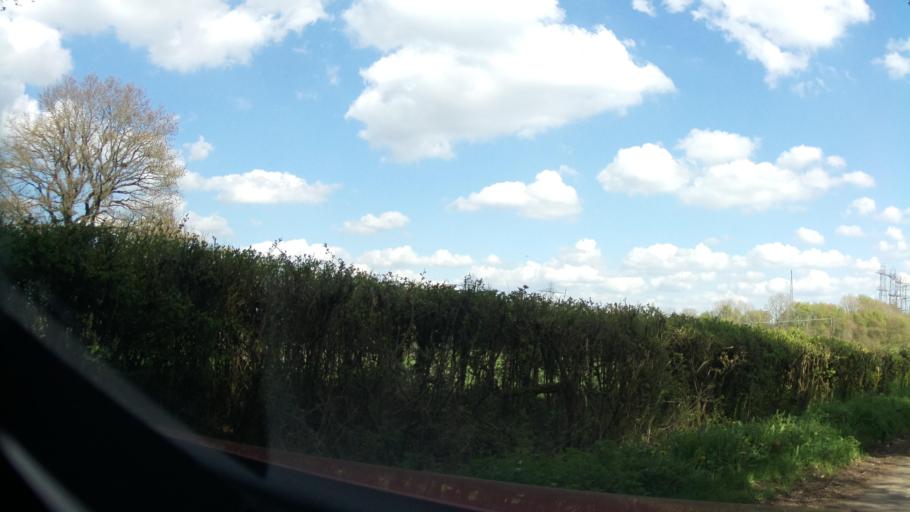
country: GB
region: England
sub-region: South Gloucestershire
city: Tytherington
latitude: 51.5695
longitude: -2.4869
